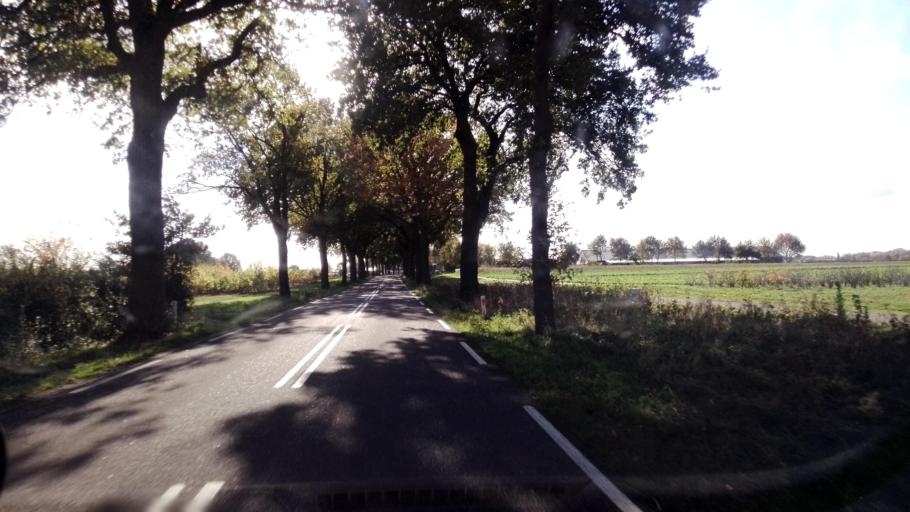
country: NL
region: Limburg
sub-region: Gemeente Venlo
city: Arcen
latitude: 51.4337
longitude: 6.1488
